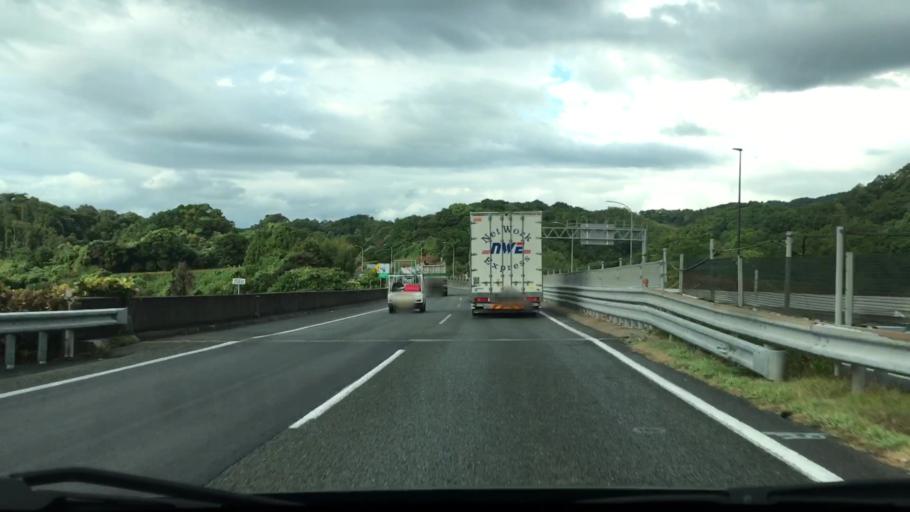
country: JP
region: Fukuoka
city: Nishifukuma
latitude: 33.7428
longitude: 130.5238
